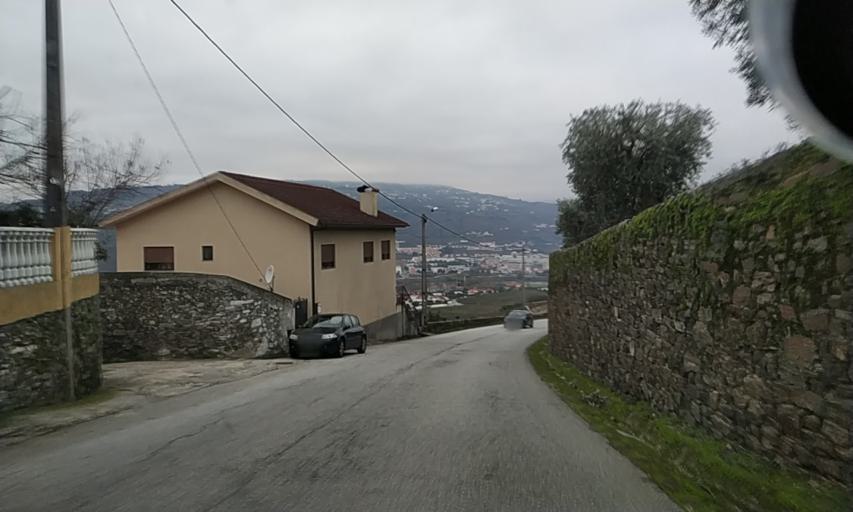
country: PT
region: Vila Real
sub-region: Peso da Regua
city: Peso da Regua
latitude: 41.1443
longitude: -7.7920
